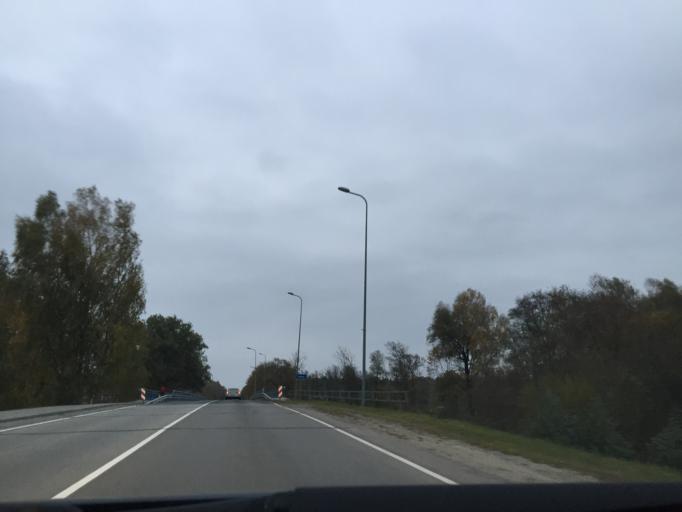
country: LV
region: Ozolnieku
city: Ozolnieki
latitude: 56.6915
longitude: 23.7969
